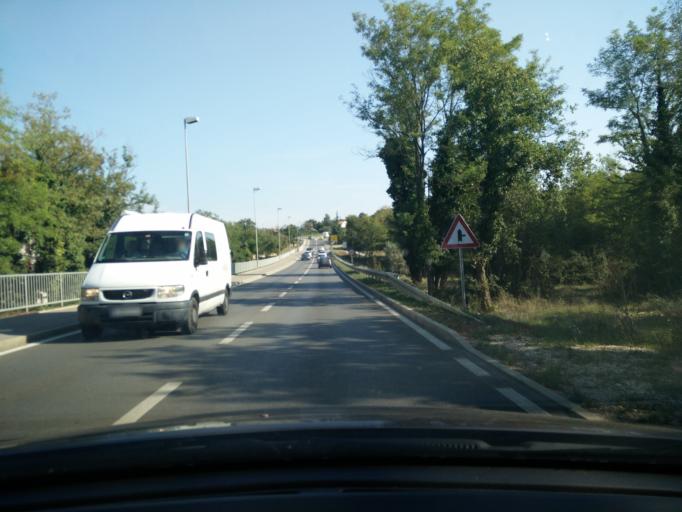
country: HR
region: Istarska
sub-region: Grad Porec
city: Porec
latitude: 45.2415
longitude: 13.6064
